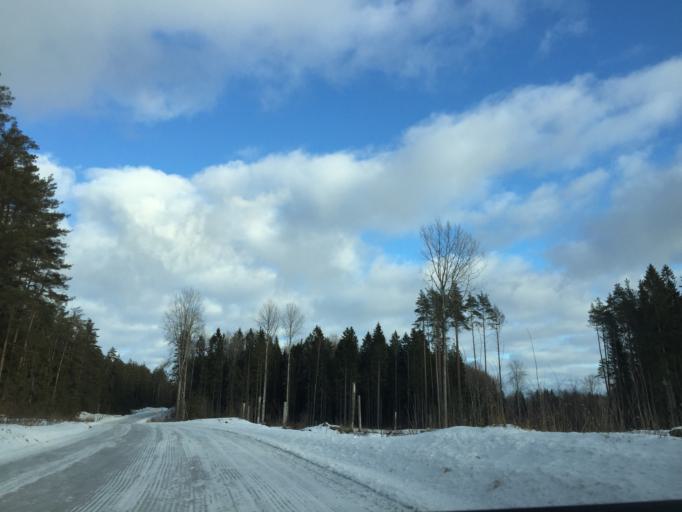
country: LV
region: Ogre
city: Jumprava
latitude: 56.5944
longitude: 24.9889
